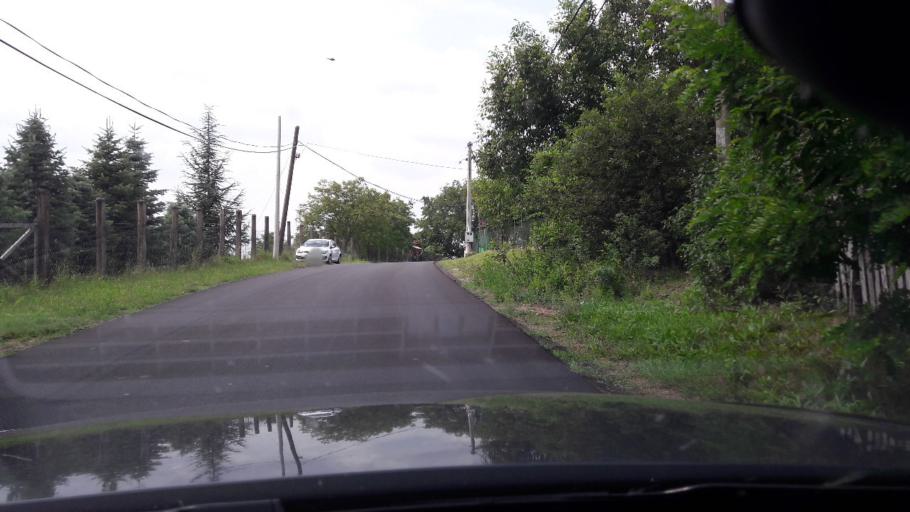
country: RS
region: Central Serbia
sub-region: Belgrade
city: Sopot
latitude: 44.6023
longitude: 20.6018
